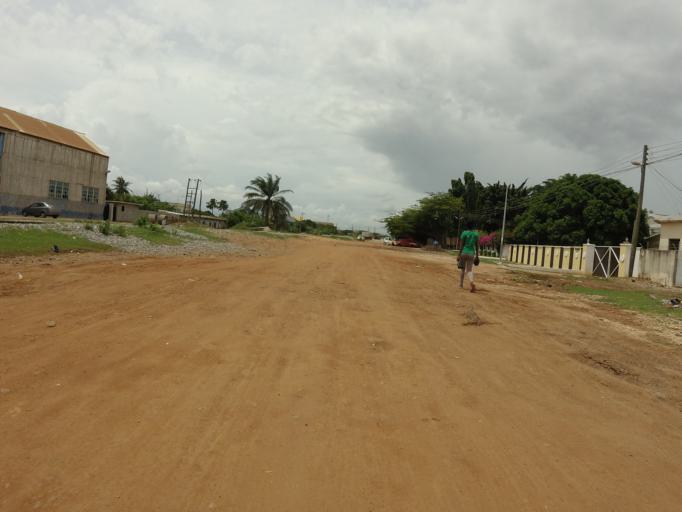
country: GH
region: Greater Accra
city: Accra
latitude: 5.6040
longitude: -0.2114
